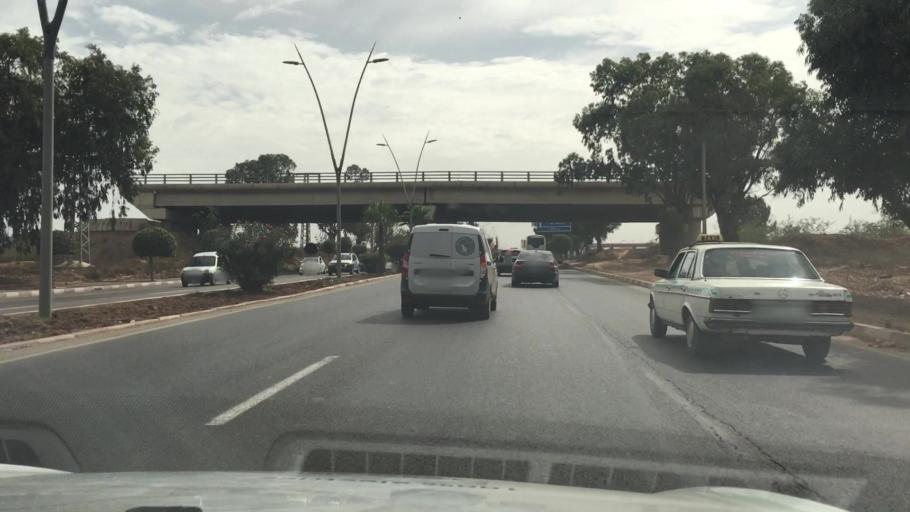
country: MA
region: Grand Casablanca
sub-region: Nouaceur
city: Bouskoura
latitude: 33.5125
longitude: -7.6309
